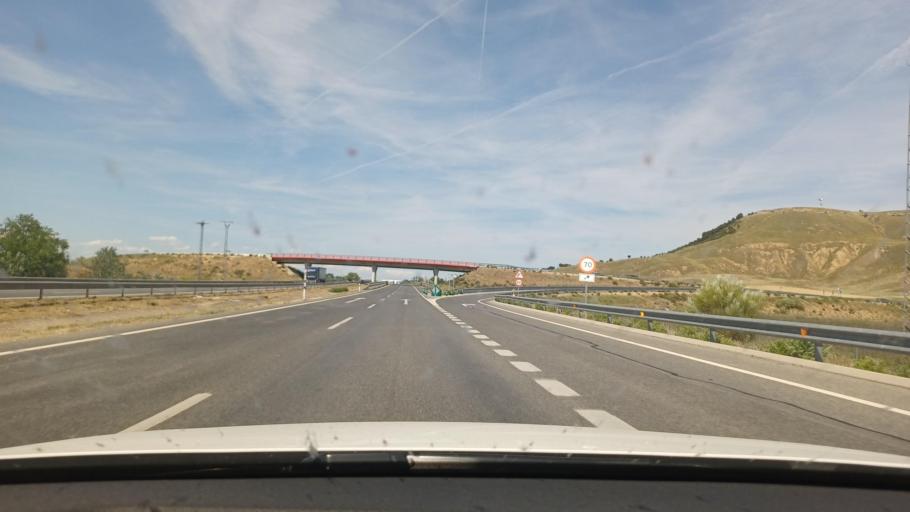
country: ES
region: Madrid
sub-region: Provincia de Madrid
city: Torrejon de Ardoz
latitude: 40.4473
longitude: -3.4227
